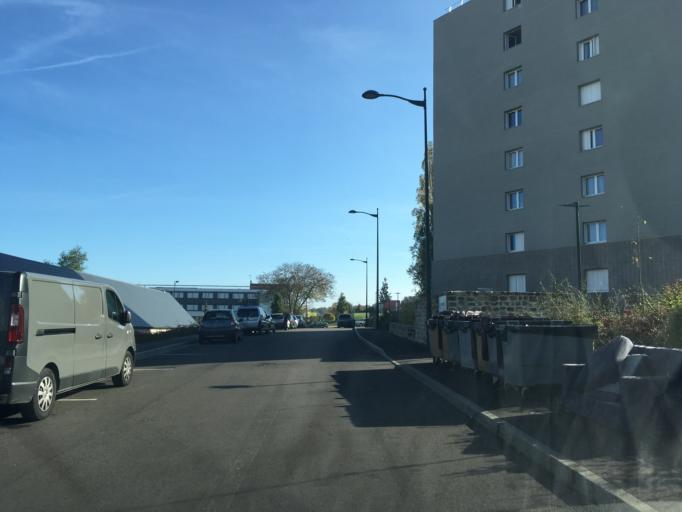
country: FR
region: Haute-Normandie
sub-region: Departement de l'Eure
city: Vernon
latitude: 49.0761
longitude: 1.4927
